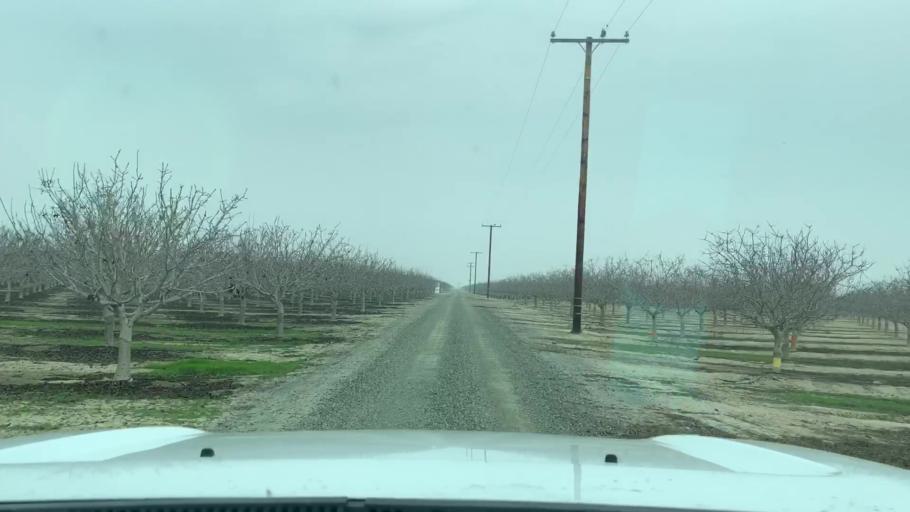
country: US
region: California
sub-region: Tulare County
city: Earlimart
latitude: 35.8208
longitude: -119.3397
